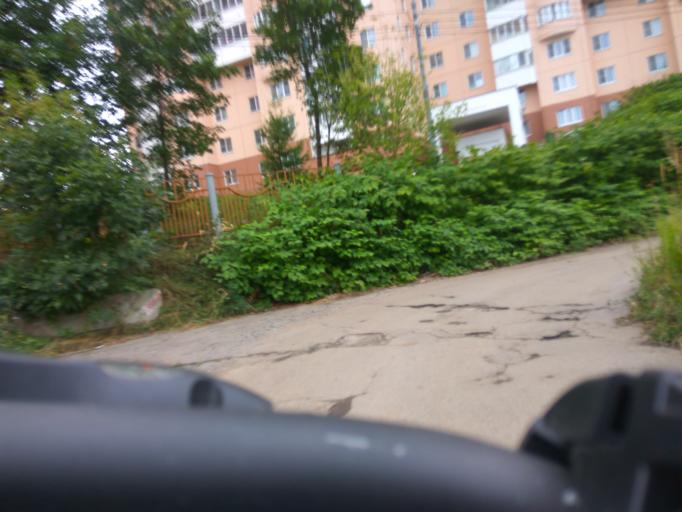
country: RU
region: Moscow
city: Tsaritsyno
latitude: 55.6452
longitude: 37.6500
